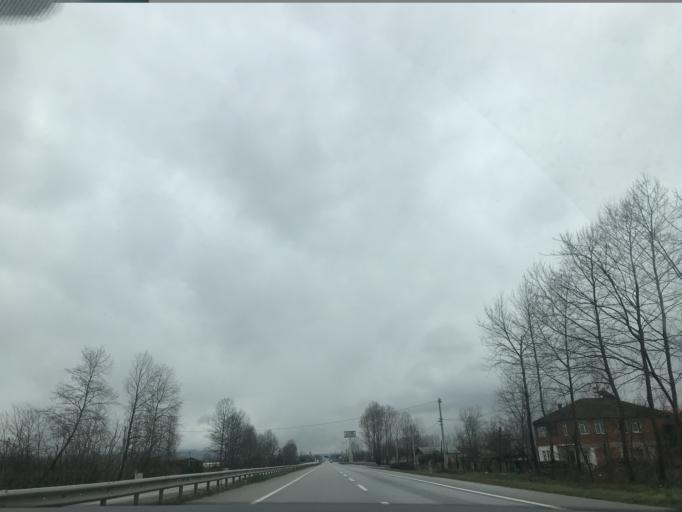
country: TR
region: Sakarya
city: Akyazi
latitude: 40.7727
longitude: 30.6386
